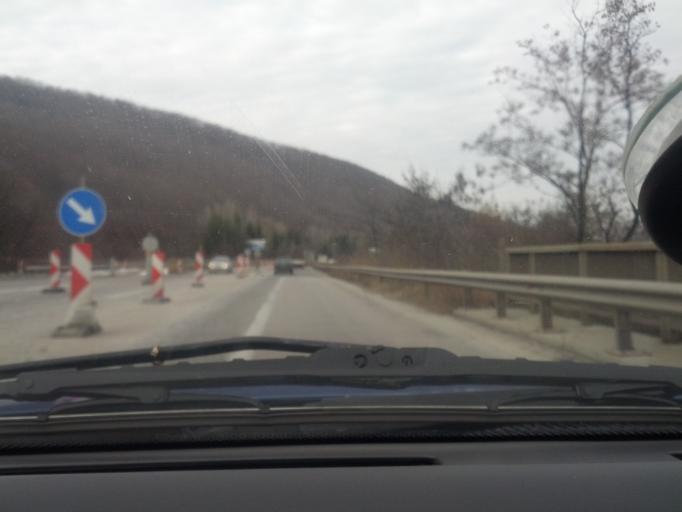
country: BG
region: Sofiya
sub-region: Obshtina Botevgrad
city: Botevgrad
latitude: 42.8096
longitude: 23.8030
